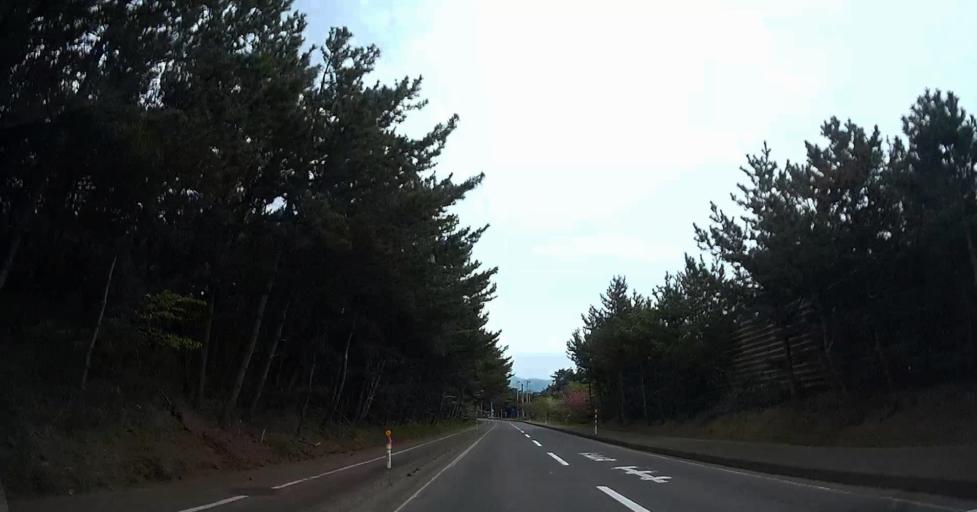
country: JP
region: Aomori
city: Shimokizukuri
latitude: 41.0418
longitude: 140.3260
